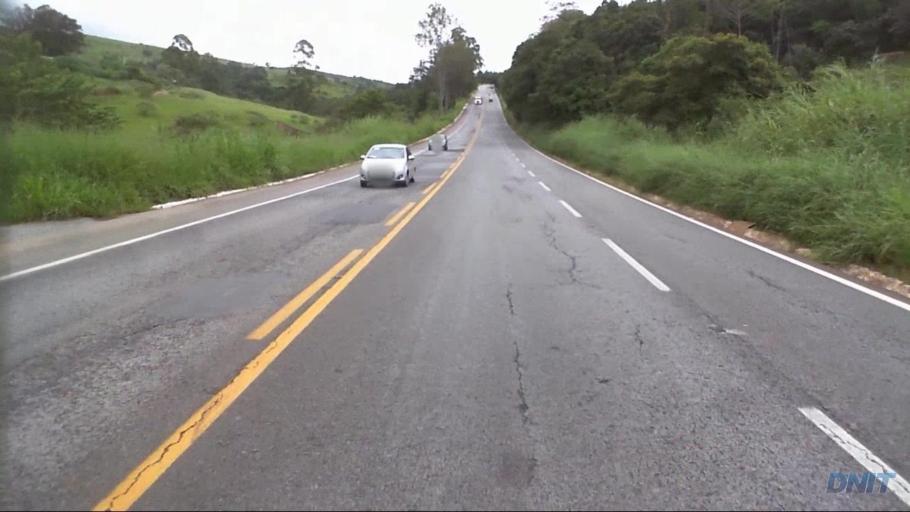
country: BR
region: Minas Gerais
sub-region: Joao Monlevade
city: Joao Monlevade
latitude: -19.8512
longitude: -43.2945
